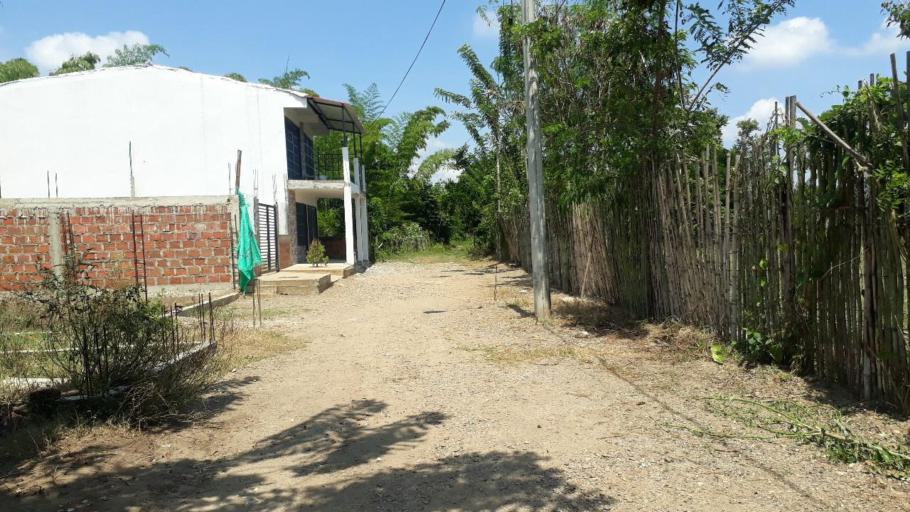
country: CO
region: Valle del Cauca
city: Jamundi
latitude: 3.1318
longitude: -76.5459
